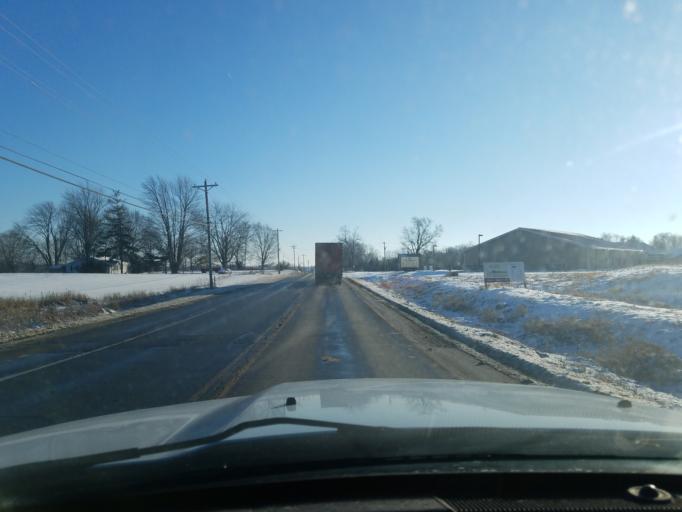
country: US
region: Indiana
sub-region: Noble County
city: Kendallville
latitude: 41.4524
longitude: -85.3079
